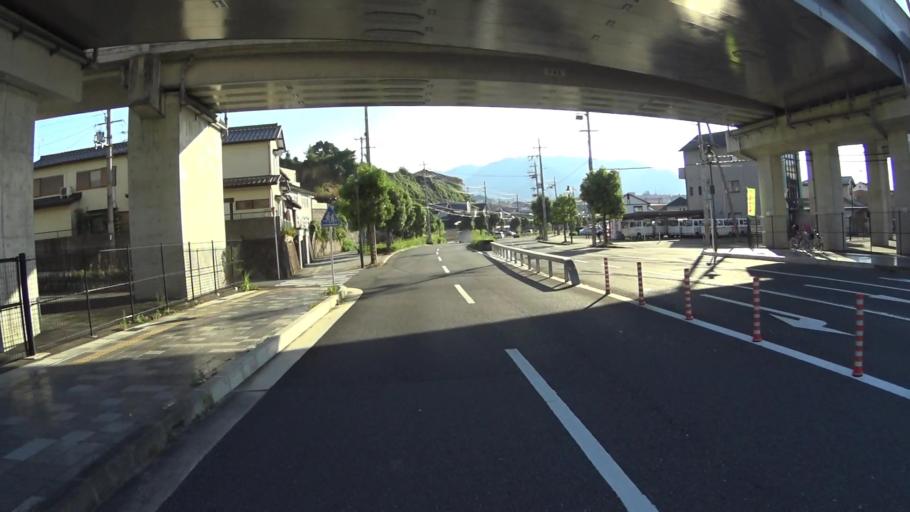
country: JP
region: Kyoto
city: Fukuchiyama
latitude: 35.2952
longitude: 135.1238
